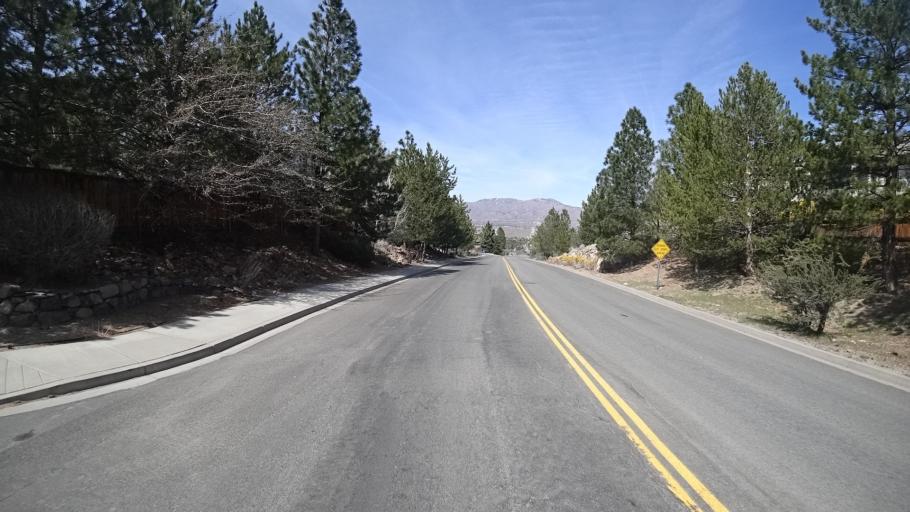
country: US
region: Nevada
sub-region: Washoe County
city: Reno
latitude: 39.4832
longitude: -119.8630
